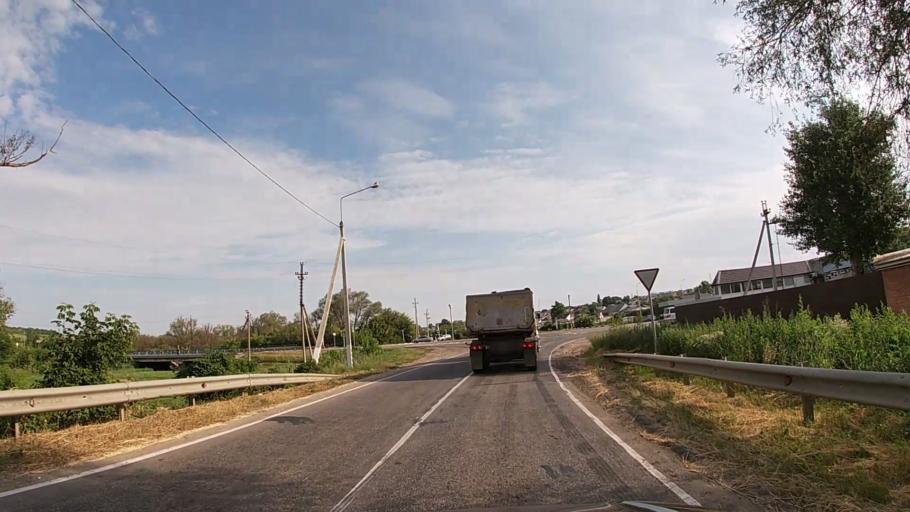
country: RU
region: Belgorod
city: Severnyy
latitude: 50.6348
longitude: 36.4642
